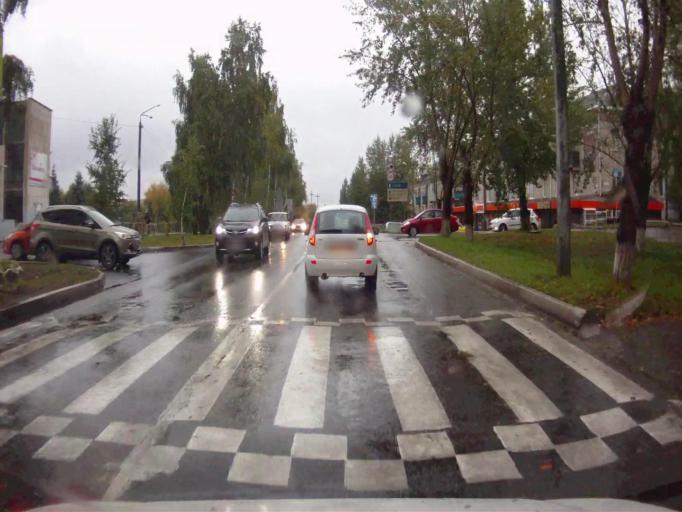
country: RU
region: Chelyabinsk
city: Kyshtym
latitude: 55.7050
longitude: 60.5564
